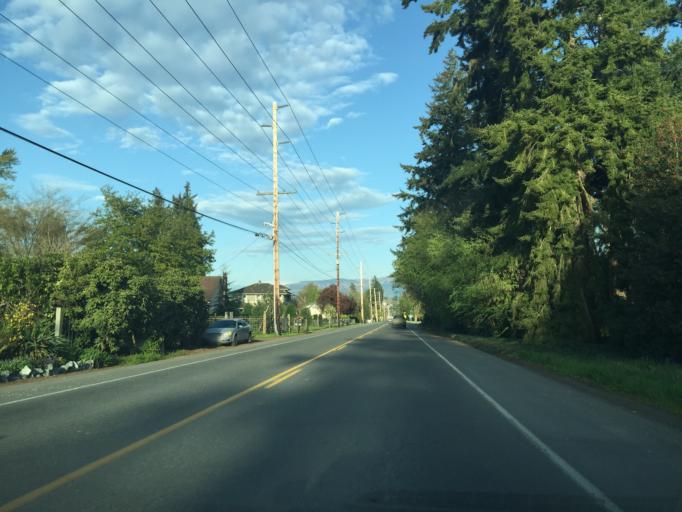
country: US
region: Washington
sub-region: Skagit County
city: Mount Vernon
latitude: 48.4207
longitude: -122.3559
